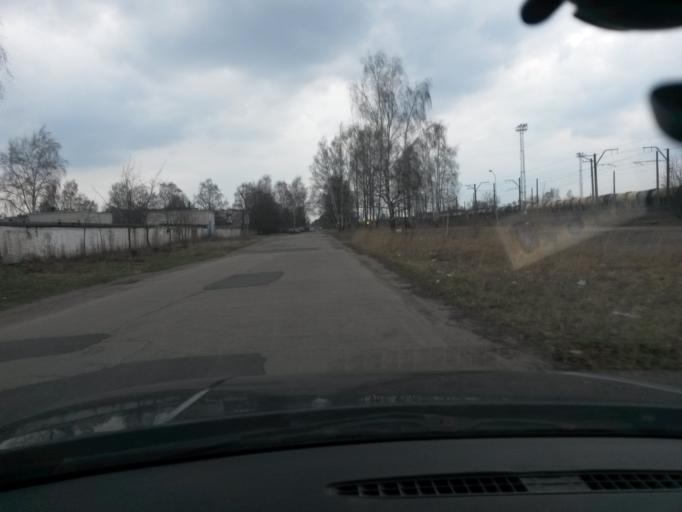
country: LV
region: Kekava
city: Kekava
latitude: 56.8991
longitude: 24.2209
